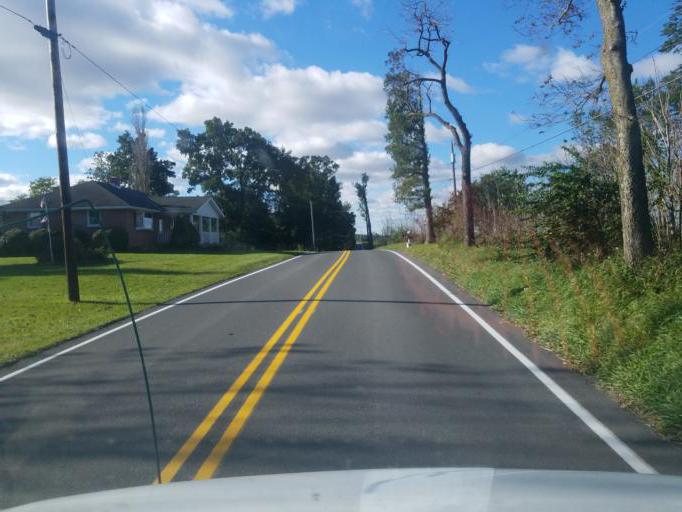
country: US
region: Pennsylvania
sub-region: Franklin County
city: Guilford Siding
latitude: 39.8195
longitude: -77.6415
